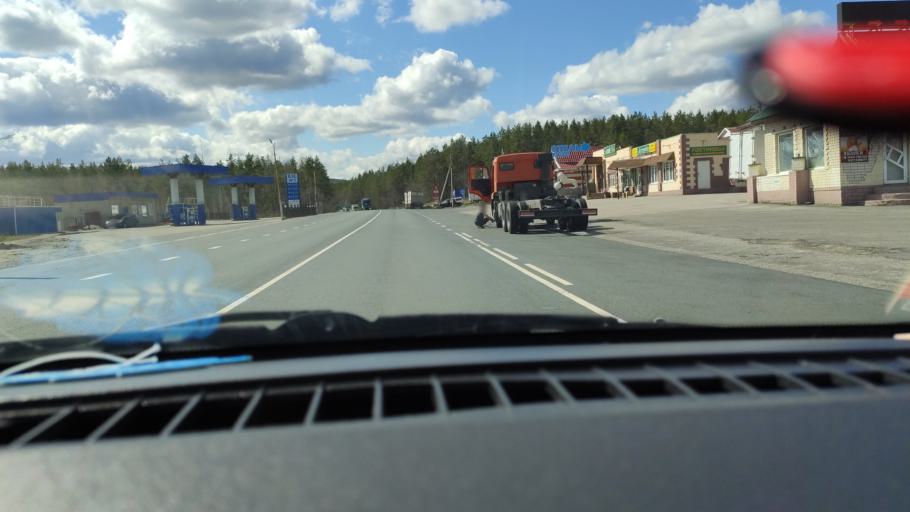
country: RU
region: Saratov
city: Khvalynsk
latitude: 52.5225
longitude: 48.0203
